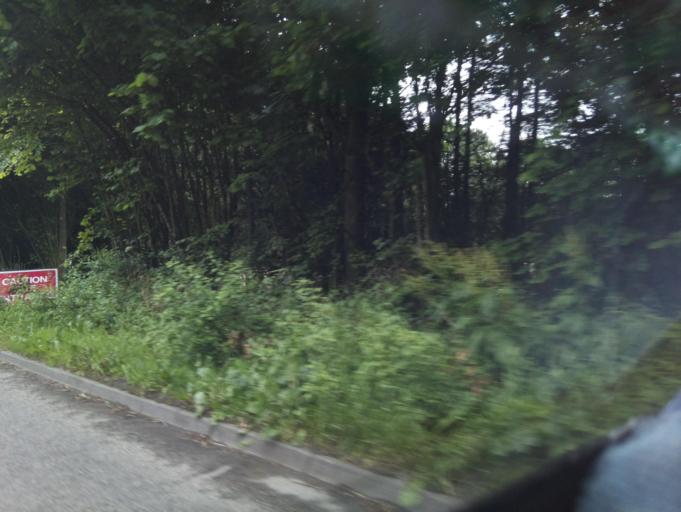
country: GB
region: England
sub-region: Derbyshire
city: Ashbourne
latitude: 53.0048
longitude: -1.7160
